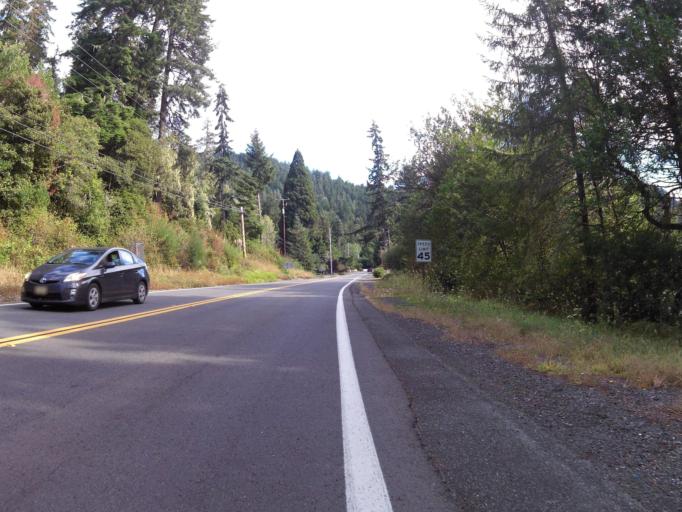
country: US
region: California
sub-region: Del Norte County
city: Bertsch-Oceanview
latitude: 41.8128
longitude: -124.0810
